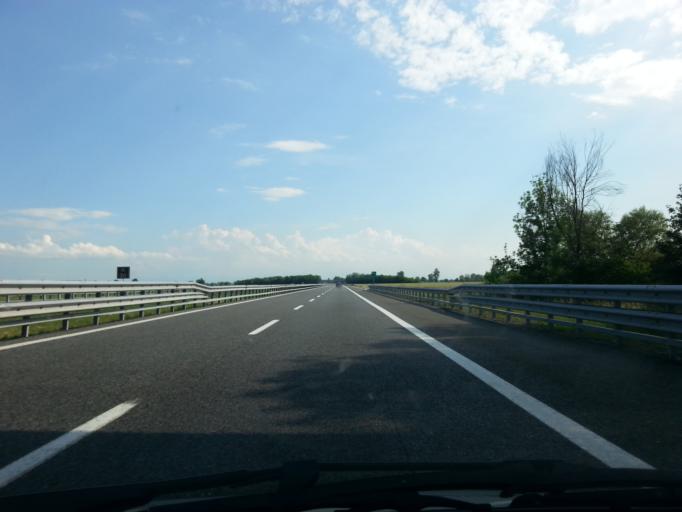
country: IT
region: Piedmont
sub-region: Provincia di Cuneo
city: Caramagna Piemonte
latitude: 44.7663
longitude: 7.7510
